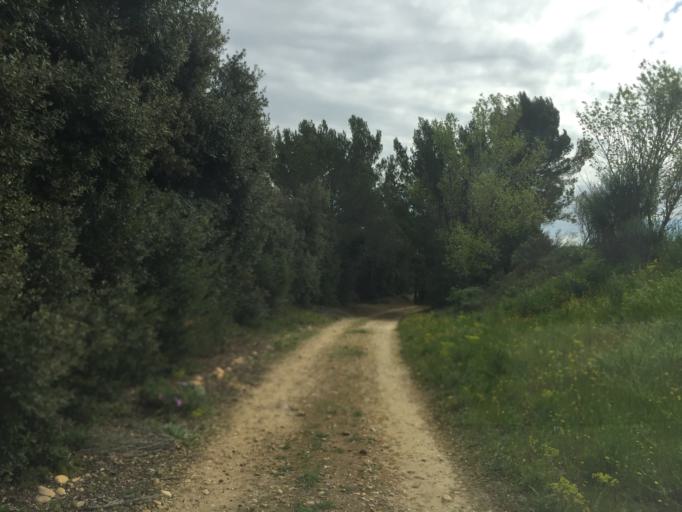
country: FR
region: Provence-Alpes-Cote d'Azur
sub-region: Departement du Vaucluse
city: Chateauneuf-du-Pape
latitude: 44.0626
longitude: 4.8540
